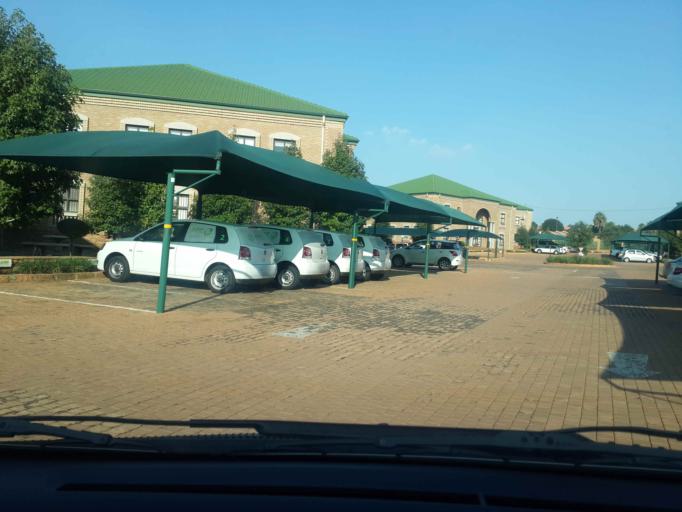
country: ZA
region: Gauteng
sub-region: City of Tshwane Metropolitan Municipality
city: Centurion
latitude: -25.8819
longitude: 28.1837
